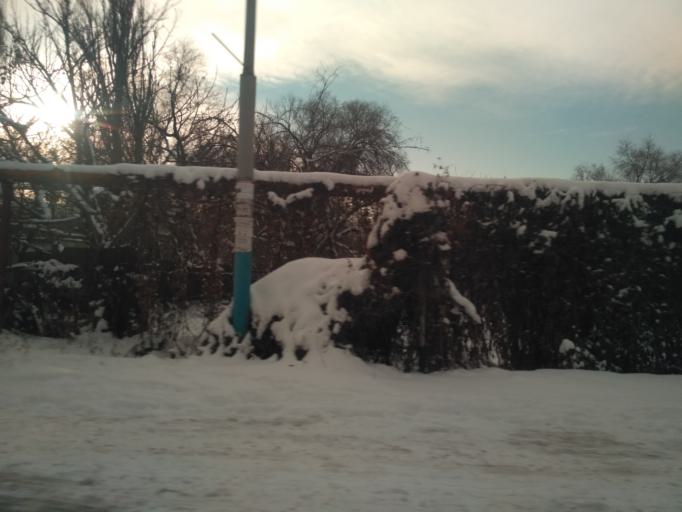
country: KZ
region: Almaty Qalasy
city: Almaty
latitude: 43.2160
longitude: 76.7664
